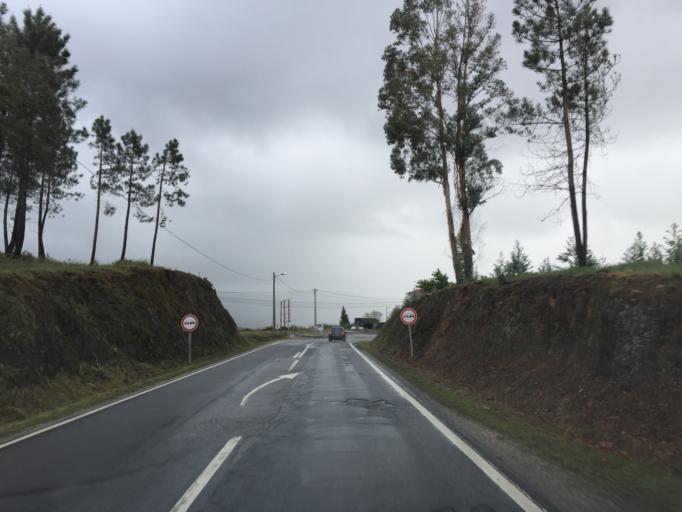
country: PT
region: Guarda
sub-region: Seia
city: Seia
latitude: 40.3879
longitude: -7.7519
